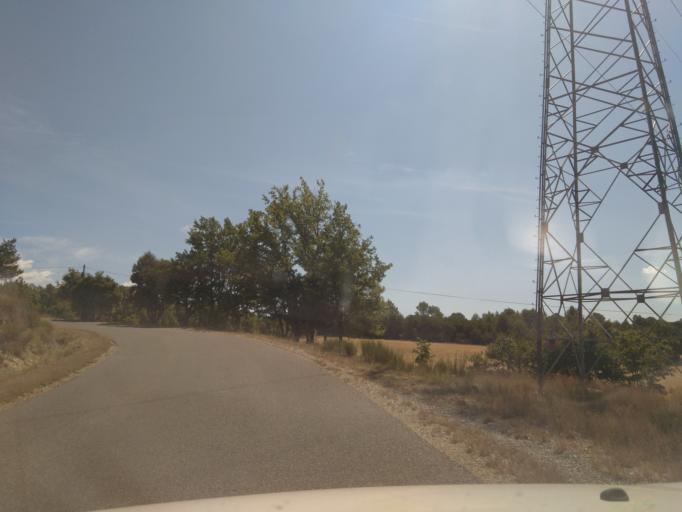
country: FR
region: Provence-Alpes-Cote d'Azur
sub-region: Departement du Var
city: Regusse
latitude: 43.7185
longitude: 6.0606
